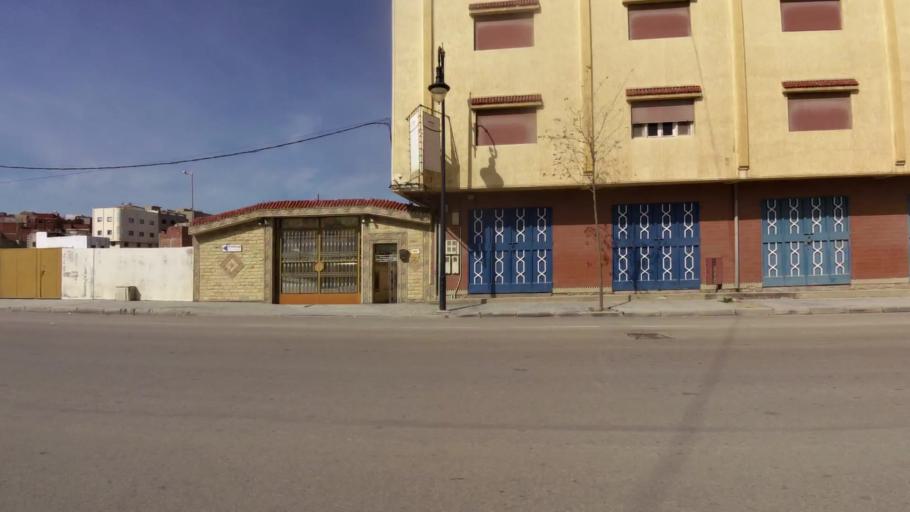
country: MA
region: Tanger-Tetouan
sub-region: Tanger-Assilah
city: Tangier
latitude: 35.7175
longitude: -5.8046
